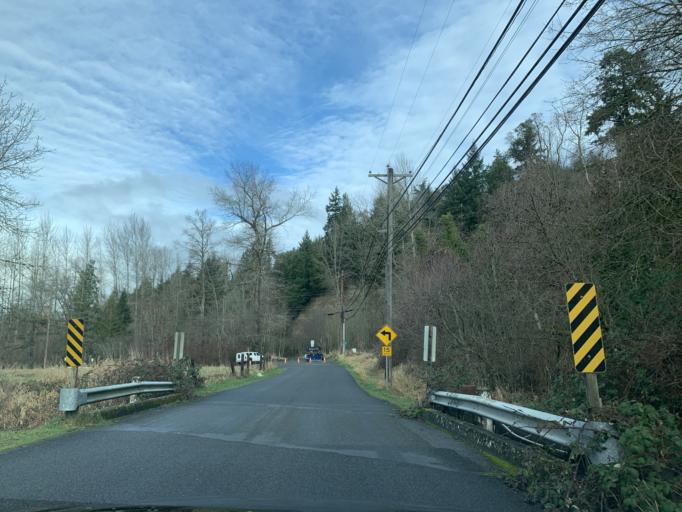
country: US
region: Washington
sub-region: Pierce County
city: Fife Heights
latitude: 47.2492
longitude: -122.3468
